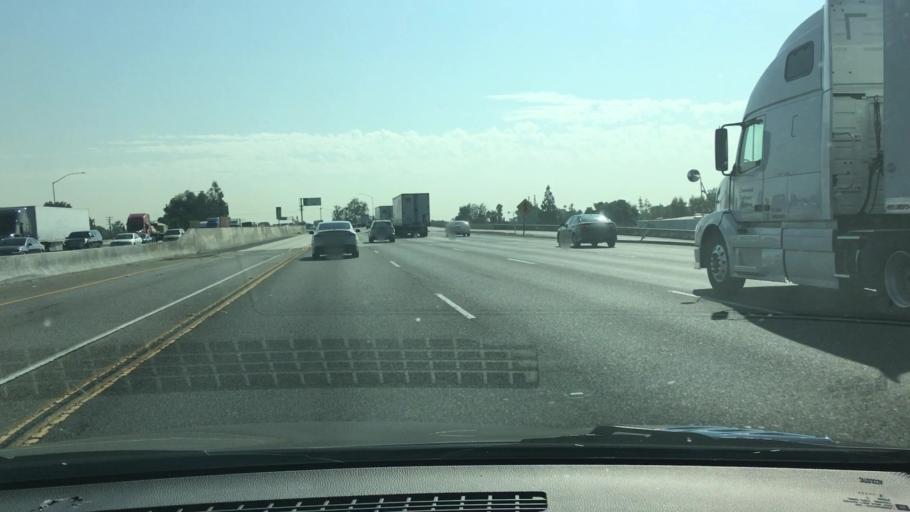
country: US
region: California
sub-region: Los Angeles County
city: Pomona
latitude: 34.0250
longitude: -117.7301
